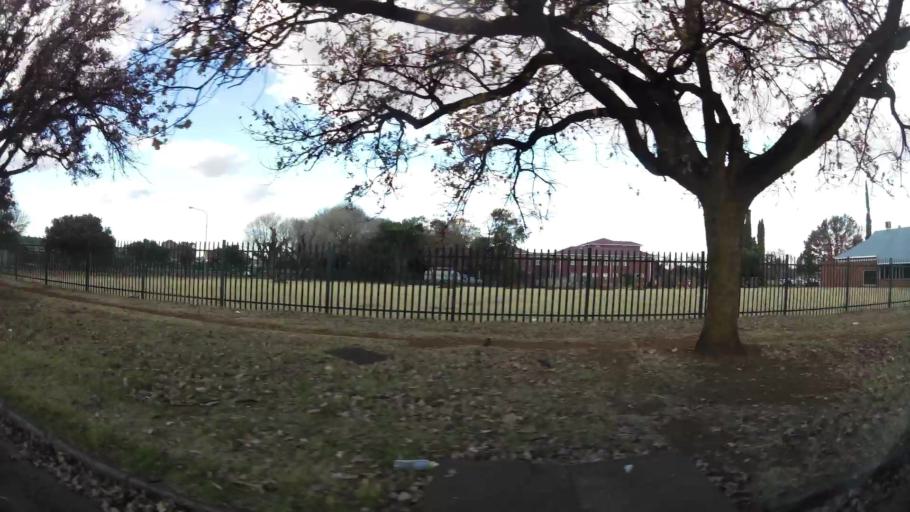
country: ZA
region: North-West
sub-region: Dr Kenneth Kaunda District Municipality
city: Potchefstroom
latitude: -26.7172
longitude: 27.0888
